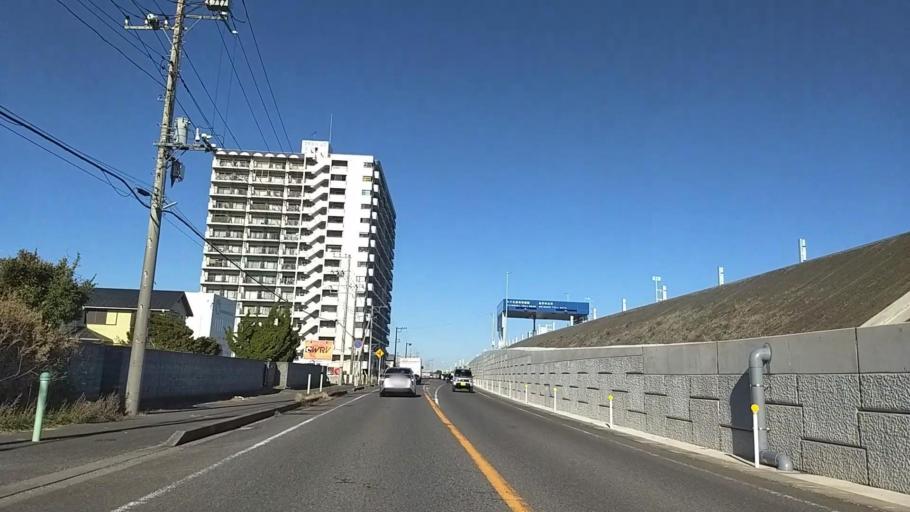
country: JP
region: Chiba
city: Togane
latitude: 35.4520
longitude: 140.4034
